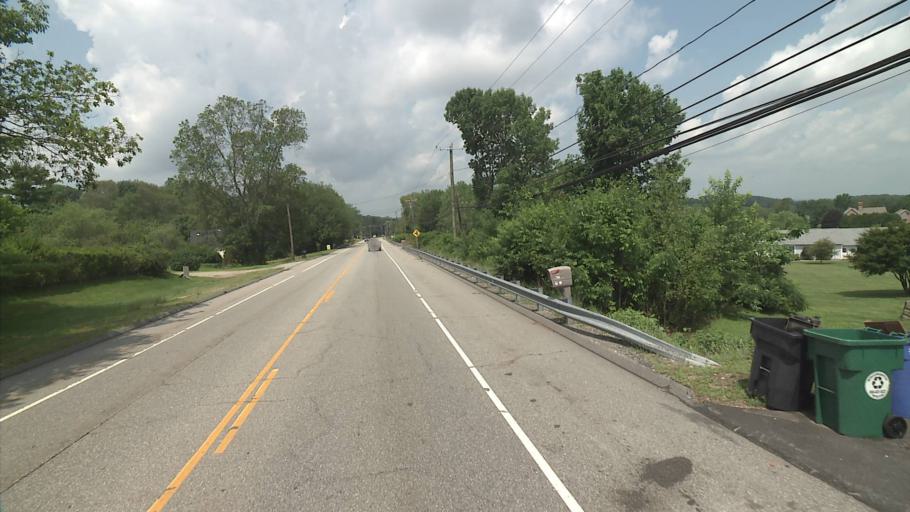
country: US
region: Connecticut
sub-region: New London County
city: Jewett City
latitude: 41.5867
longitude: -71.9492
